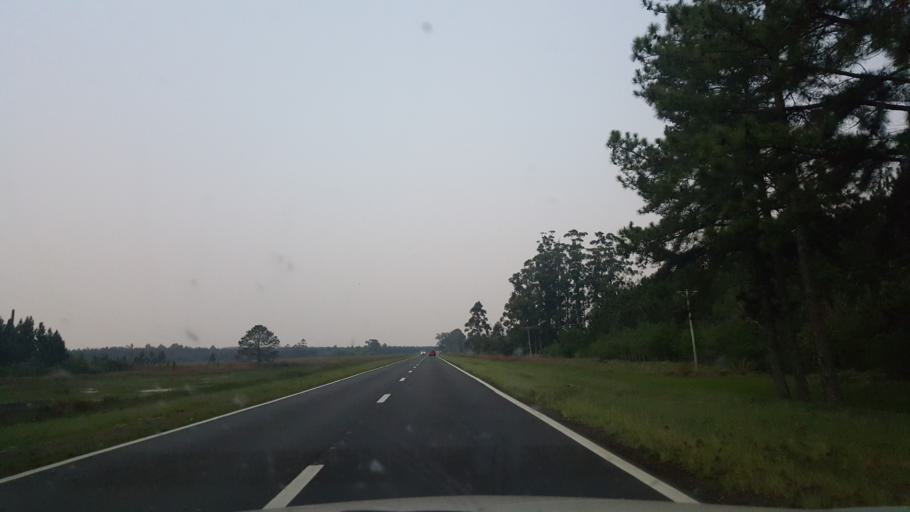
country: PY
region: Misiones
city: Ayolas
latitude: -27.6256
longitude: -56.9239
